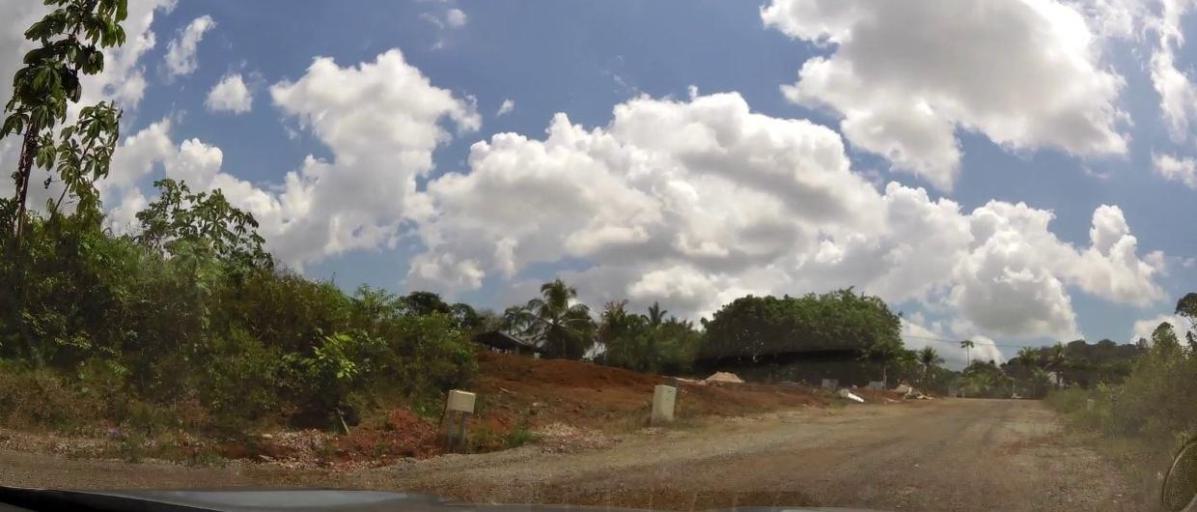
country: GF
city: Macouria
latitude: 4.8782
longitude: -52.3597
